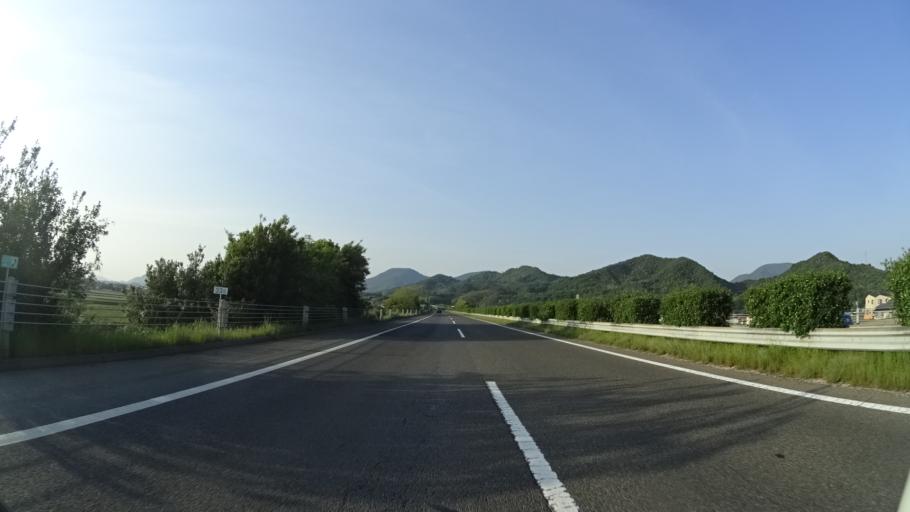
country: JP
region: Kagawa
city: Kan'onjicho
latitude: 34.1689
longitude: 133.7325
